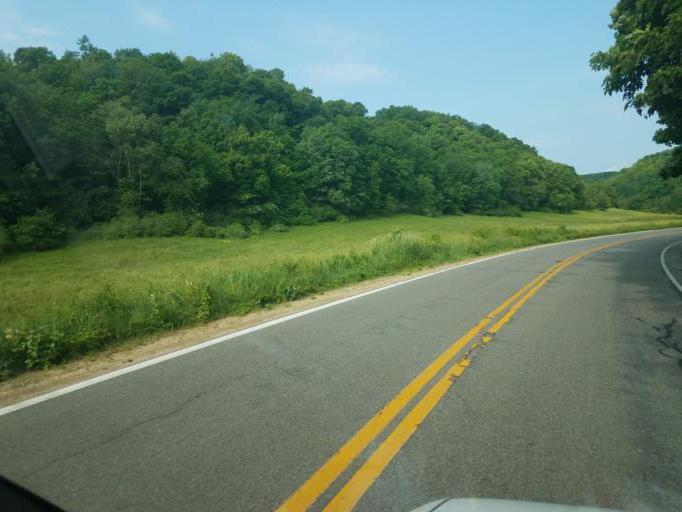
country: US
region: Wisconsin
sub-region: Vernon County
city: Hillsboro
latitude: 43.6742
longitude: -90.4843
